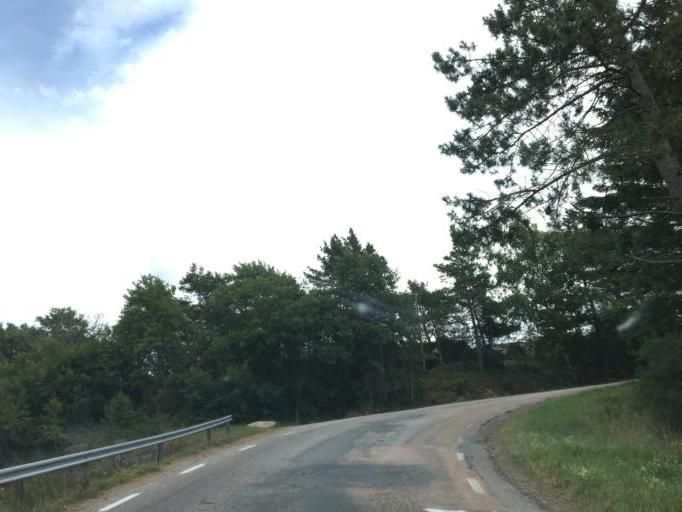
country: SE
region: Vaestra Goetaland
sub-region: Sotenas Kommun
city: Hunnebostrand
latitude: 58.4119
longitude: 11.2755
